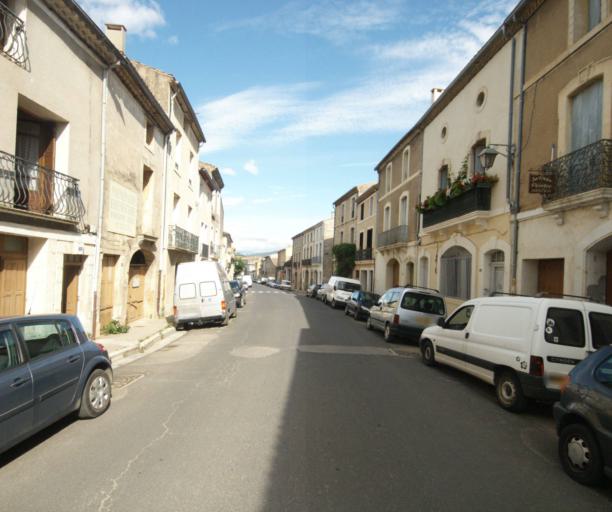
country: FR
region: Languedoc-Roussillon
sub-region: Departement de l'Herault
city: Aniane
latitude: 43.6850
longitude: 3.5891
